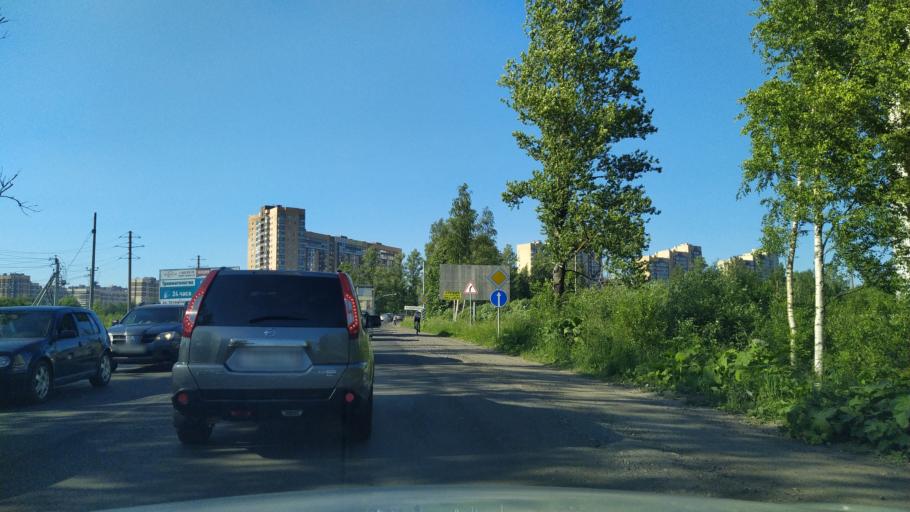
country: RU
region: Leningrad
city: Murino
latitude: 60.0525
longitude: 30.4657
